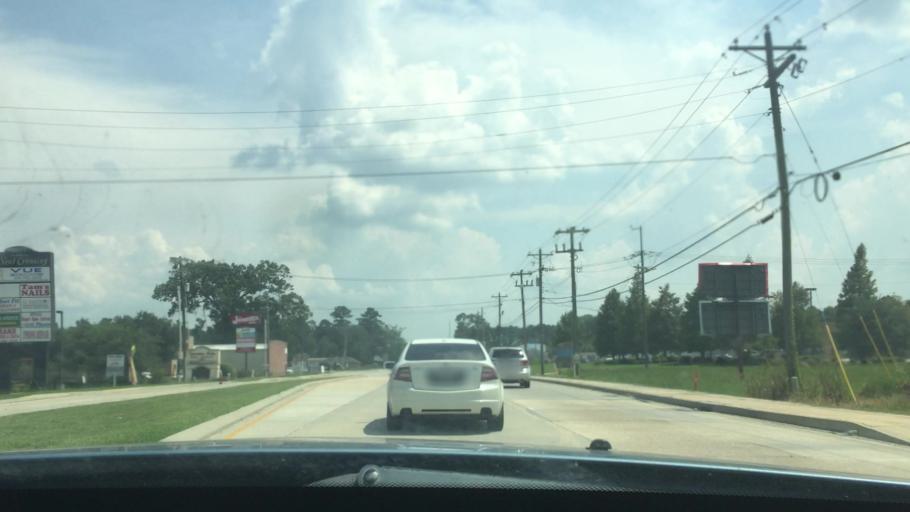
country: US
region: Louisiana
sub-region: East Baton Rouge Parish
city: Shenandoah
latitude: 30.4328
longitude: -91.0076
